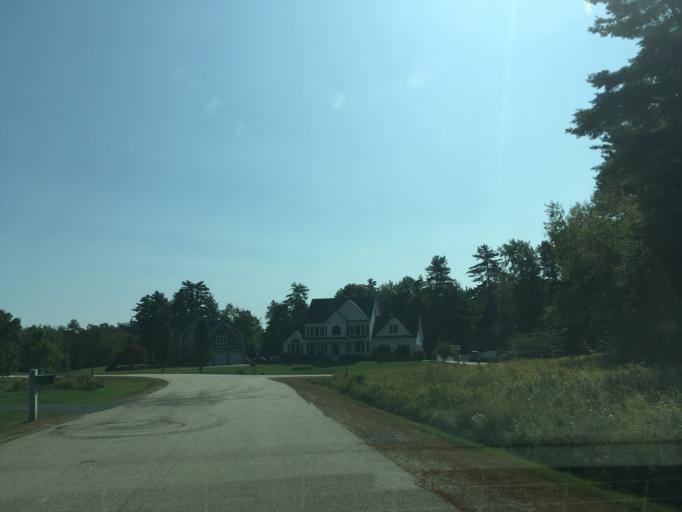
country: US
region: New Hampshire
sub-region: Rockingham County
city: Stratham Station
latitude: 43.0046
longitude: -70.8898
